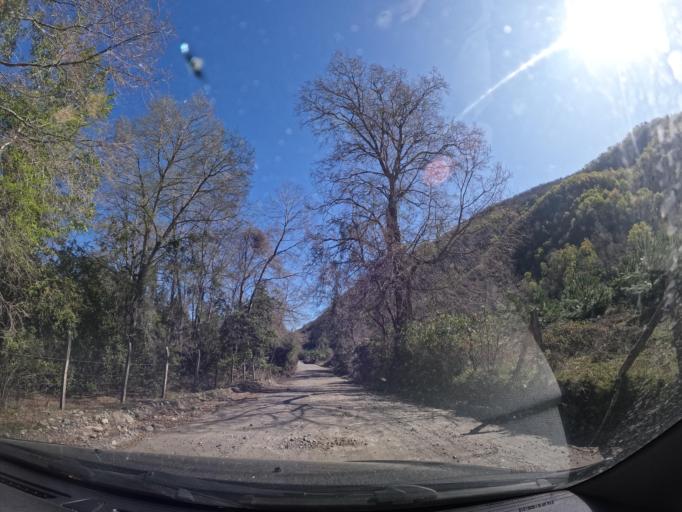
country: CL
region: Maule
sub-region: Provincia de Linares
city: Longavi
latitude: -36.2280
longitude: -71.3940
